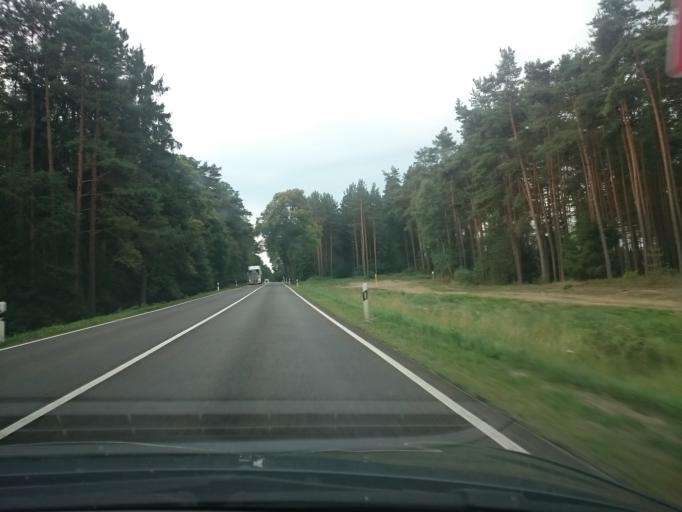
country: DE
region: Mecklenburg-Vorpommern
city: Neustrelitz
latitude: 53.2873
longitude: 13.1094
